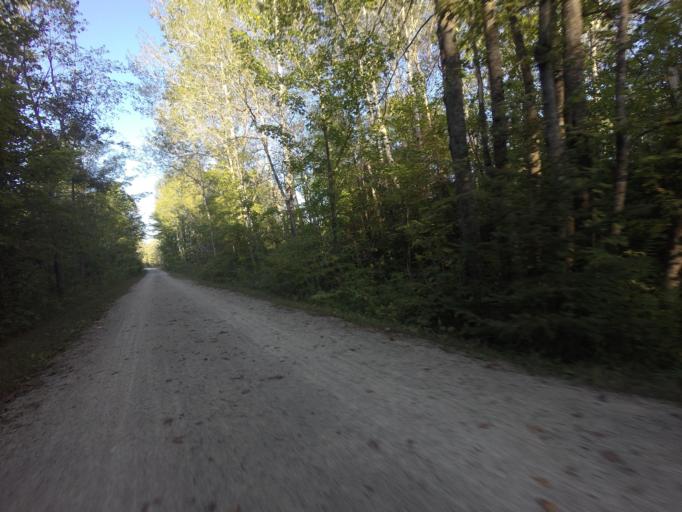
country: CA
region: Ontario
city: Brampton
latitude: 43.8332
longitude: -79.8978
